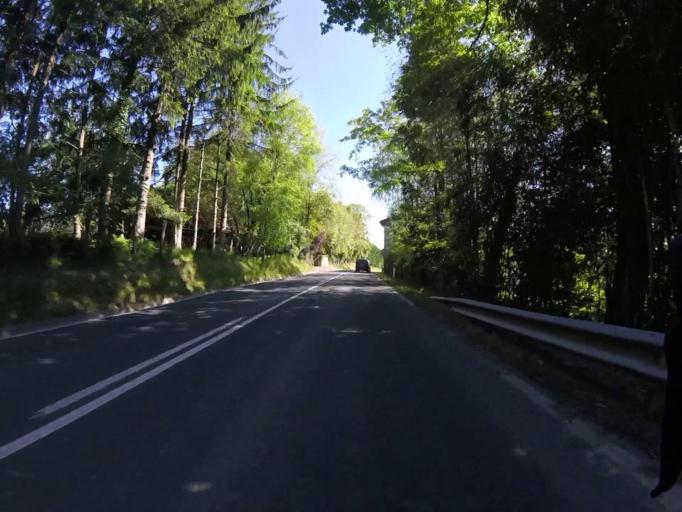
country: ES
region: Basque Country
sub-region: Provincia de Guipuzcoa
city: Irun
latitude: 43.3142
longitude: -1.8390
